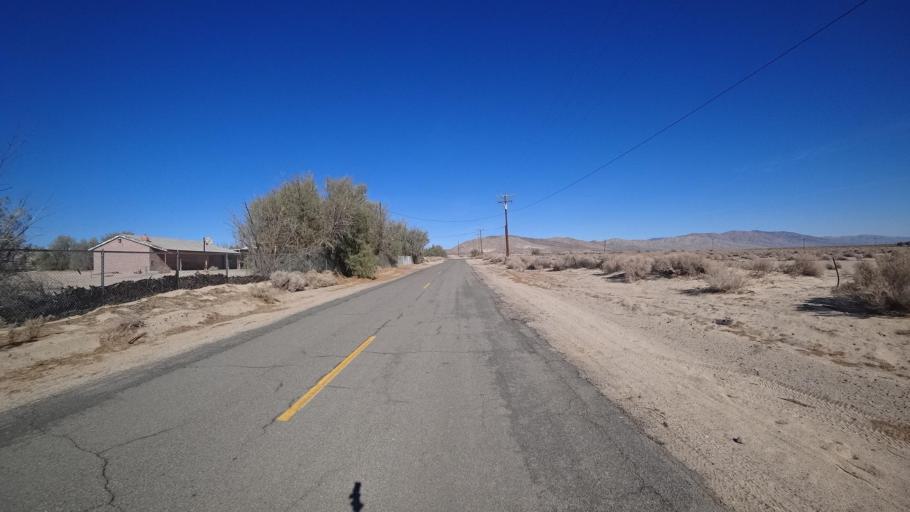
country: US
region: California
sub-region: Kern County
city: California City
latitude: 35.3067
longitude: -117.9683
